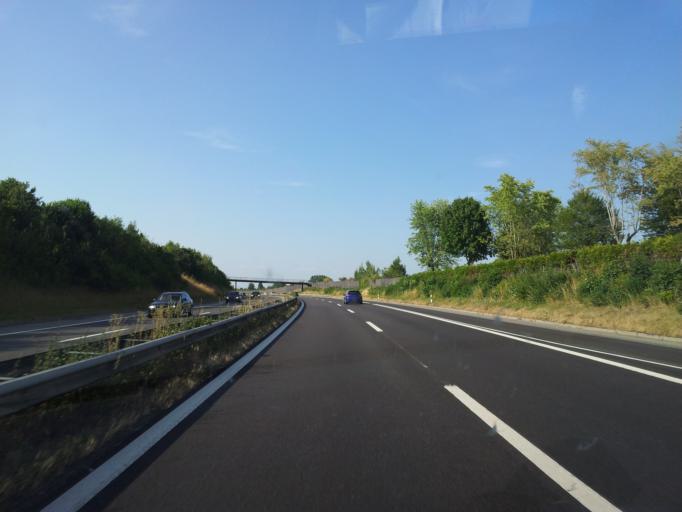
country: CH
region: Fribourg
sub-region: Sarine District
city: Matran
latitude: 46.7543
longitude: 7.0906
